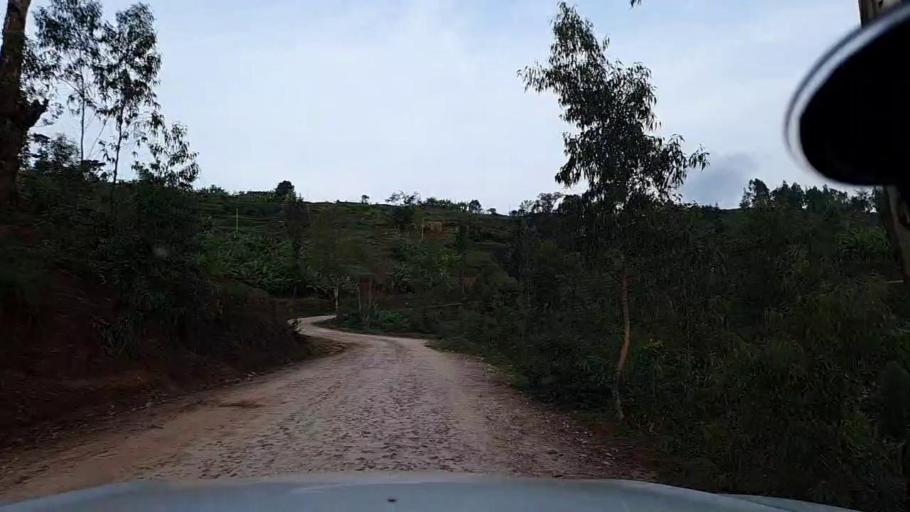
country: RW
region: Southern Province
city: Nyanza
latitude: -2.2122
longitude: 29.6322
